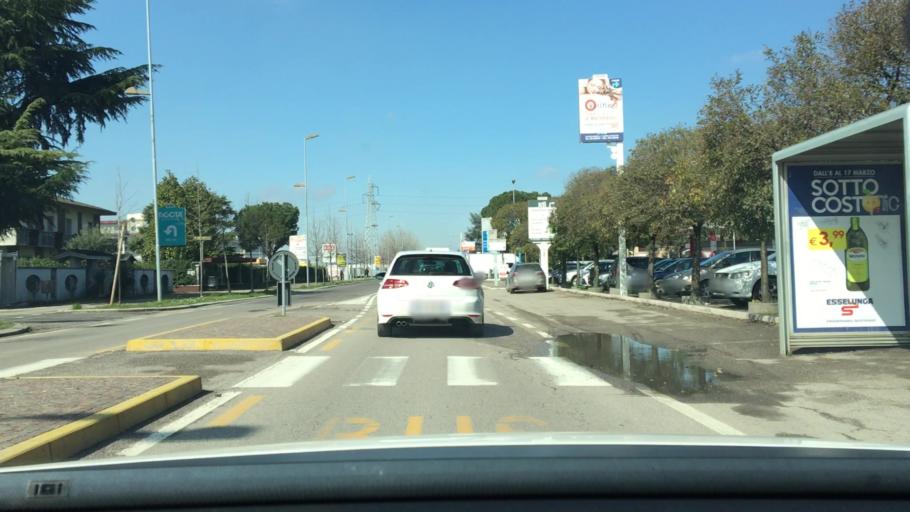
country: IT
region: Veneto
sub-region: Provincia di Verona
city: San Giovanni Lupatoto
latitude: 45.3956
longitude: 11.0276
